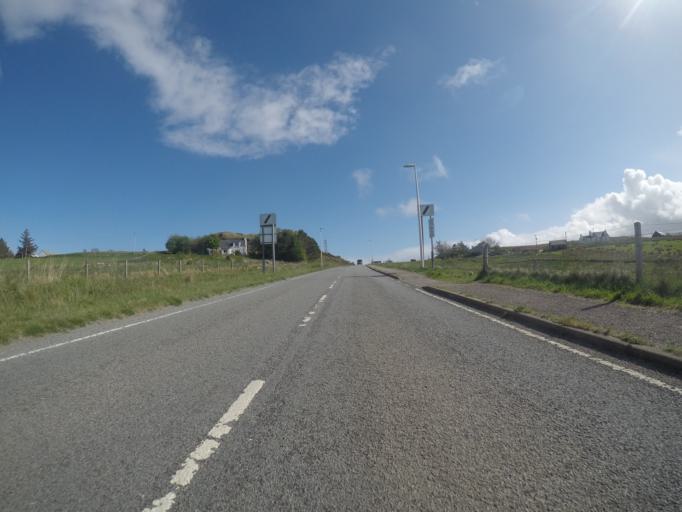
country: GB
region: Scotland
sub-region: Highland
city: Portree
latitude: 57.6220
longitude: -6.1989
